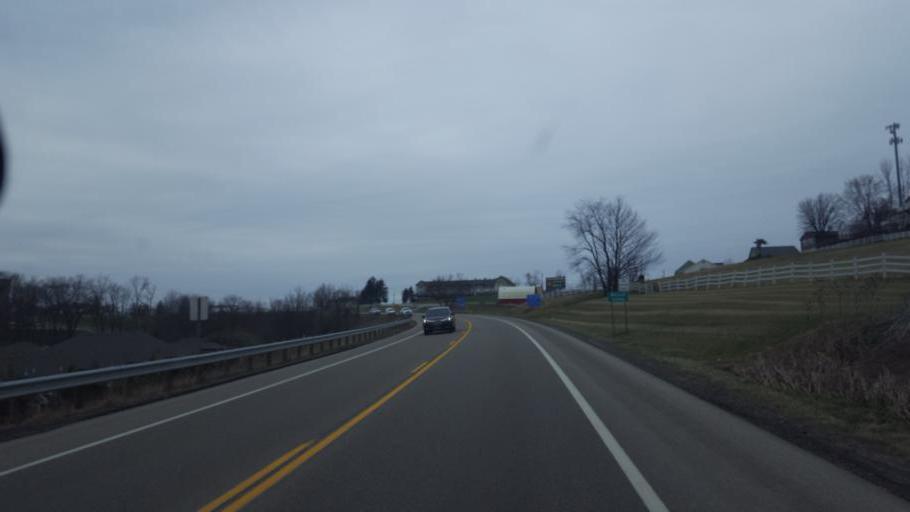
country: US
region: Ohio
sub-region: Tuscarawas County
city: Sugarcreek
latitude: 40.5380
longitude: -81.7226
